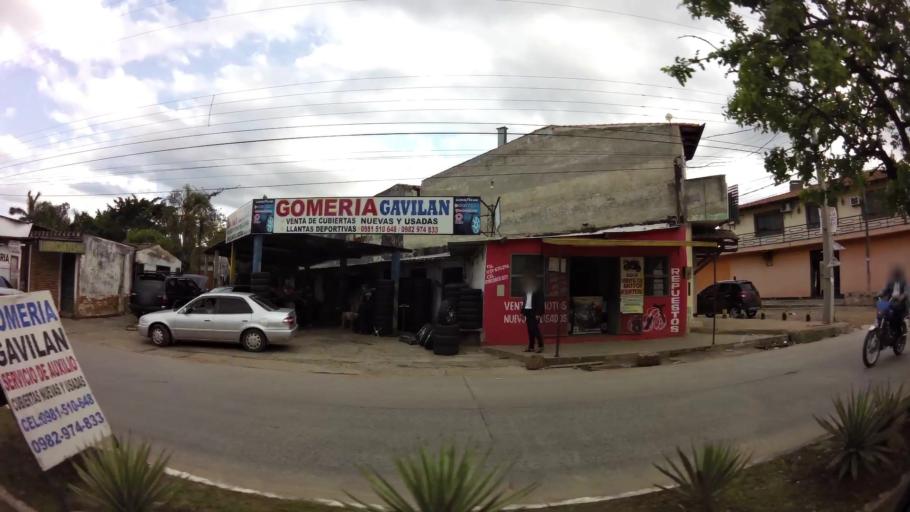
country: PY
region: Central
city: Fernando de la Mora
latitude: -25.2811
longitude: -57.5259
